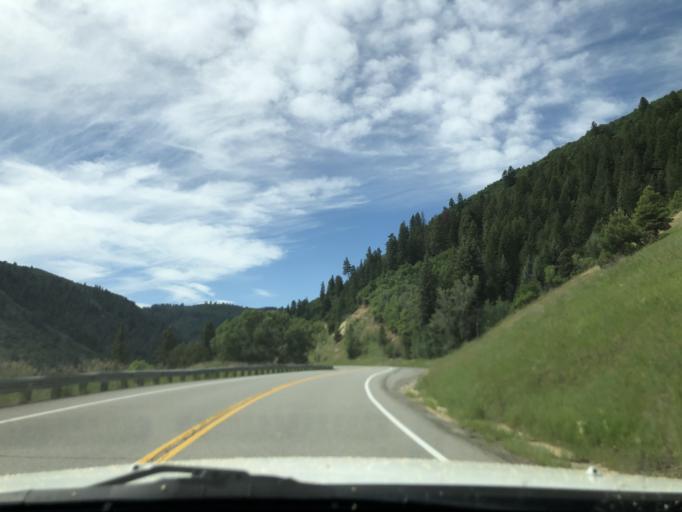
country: US
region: Colorado
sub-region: Delta County
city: Paonia
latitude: 38.9708
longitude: -107.3407
